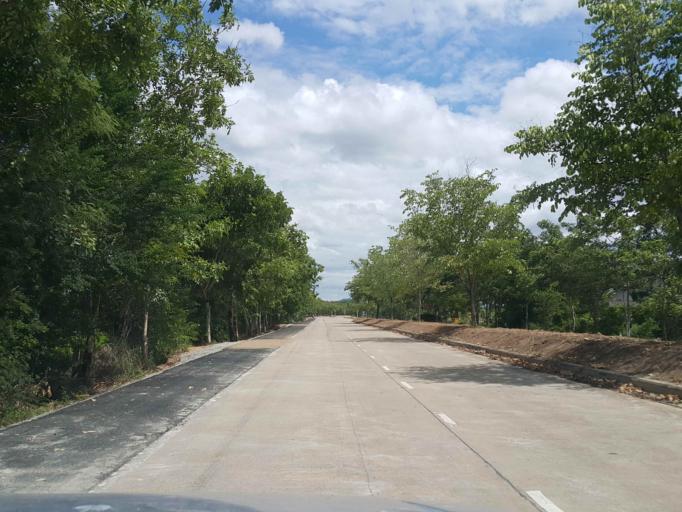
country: TH
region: Tak
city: Tak
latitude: 16.8749
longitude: 99.1116
